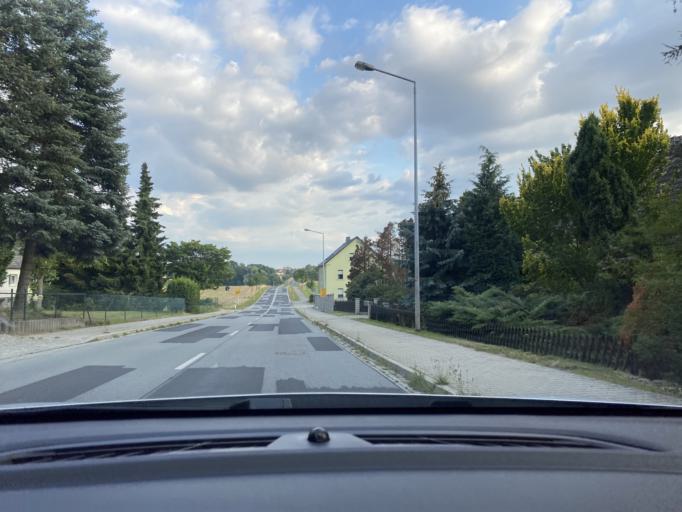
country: DE
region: Saxony
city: Radibor
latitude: 51.2216
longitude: 14.3886
